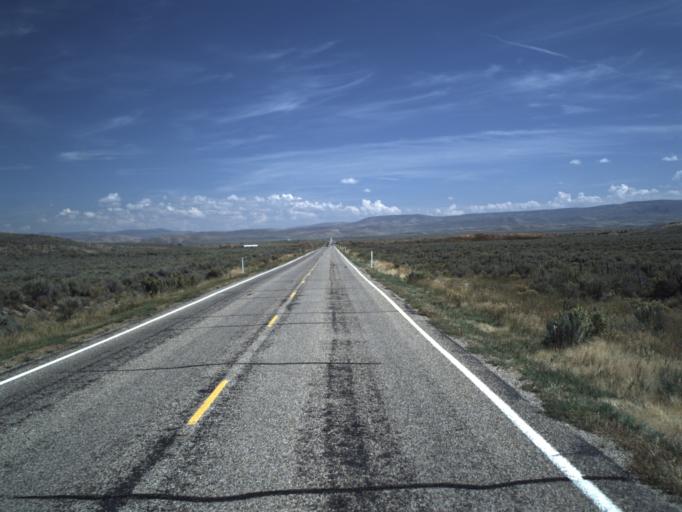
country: US
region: Utah
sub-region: Rich County
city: Randolph
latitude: 41.7708
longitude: -111.1409
